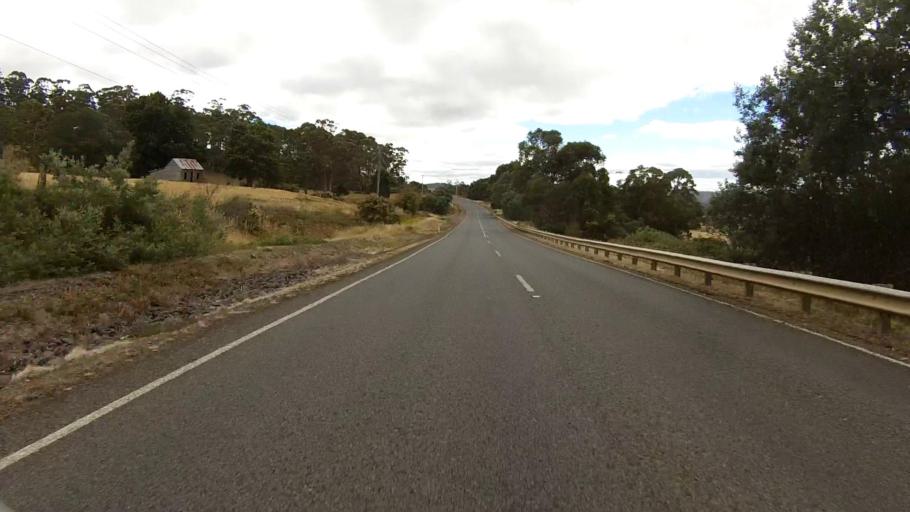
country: AU
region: Tasmania
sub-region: Sorell
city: Sorell
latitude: -42.6608
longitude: 147.5342
